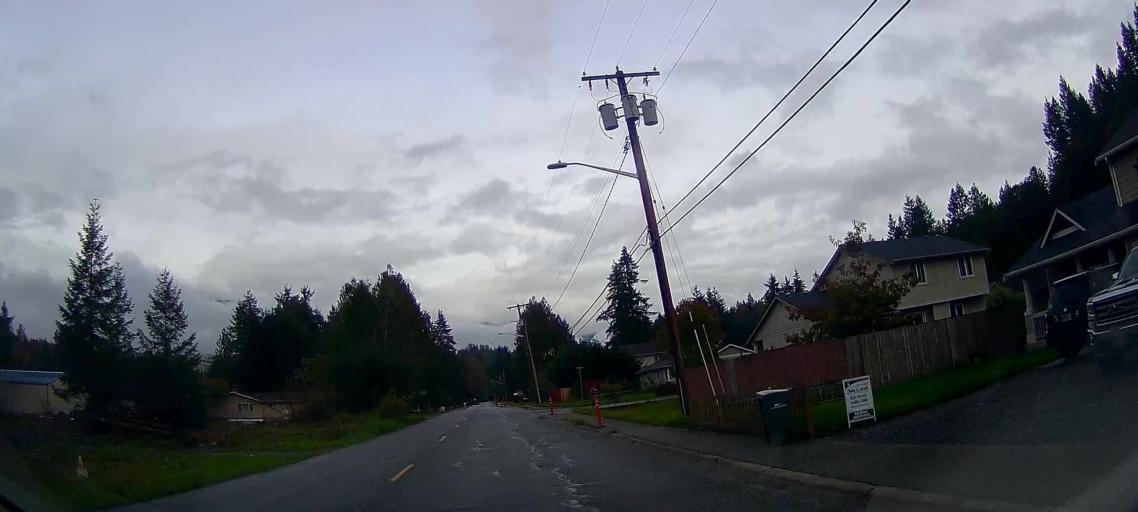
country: US
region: Washington
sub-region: Snohomish County
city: Darrington
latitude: 48.5347
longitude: -121.7647
